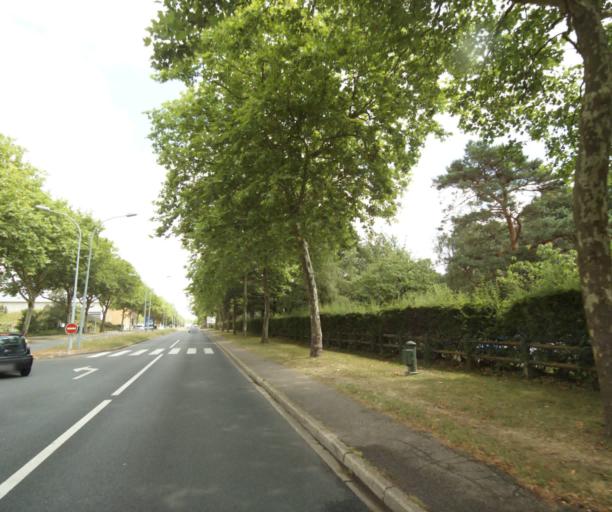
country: FR
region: Centre
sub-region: Departement du Loiret
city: Saint-Cyr-en-Val
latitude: 47.8316
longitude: 1.9385
